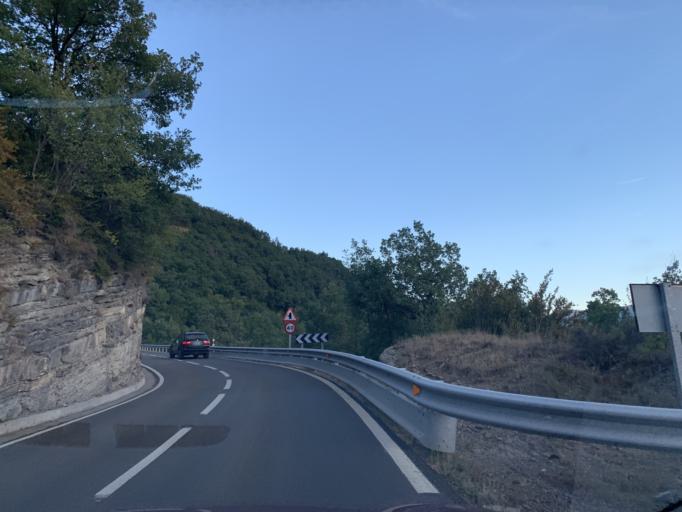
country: ES
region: Aragon
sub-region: Provincia de Huesca
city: Broto
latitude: 42.5959
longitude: -0.1188
